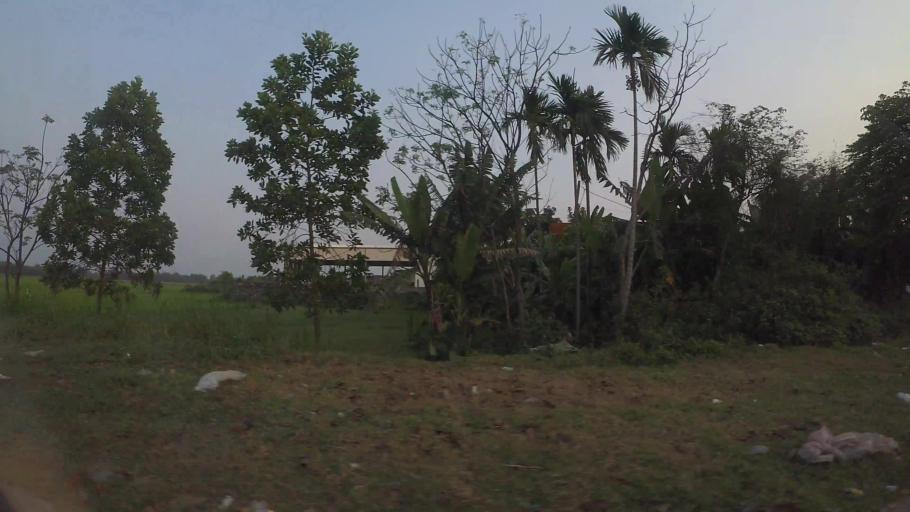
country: VN
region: Da Nang
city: Cam Le
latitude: 15.9667
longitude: 108.2118
